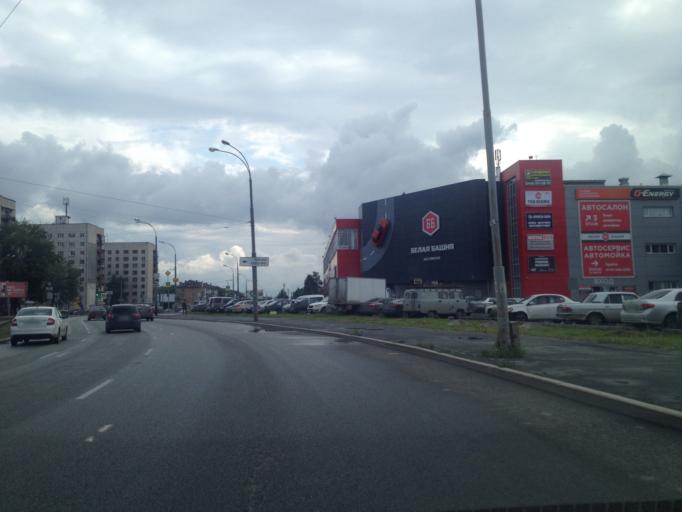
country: RU
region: Sverdlovsk
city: Yekaterinburg
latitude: 56.8934
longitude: 60.5719
